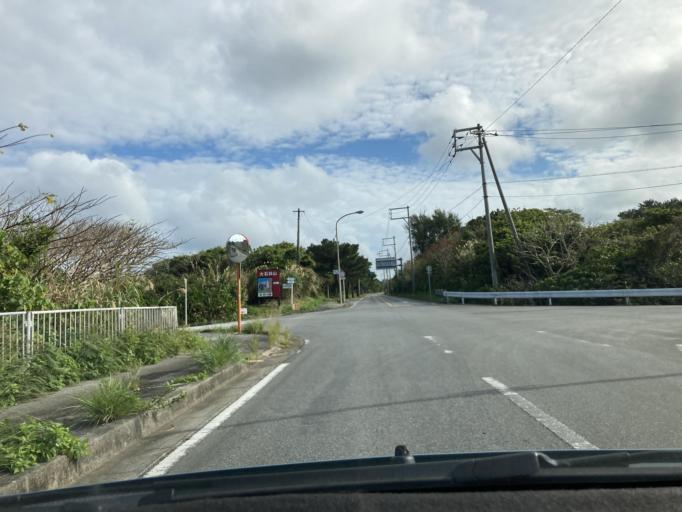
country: JP
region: Okinawa
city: Nago
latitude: 26.8666
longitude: 128.2567
